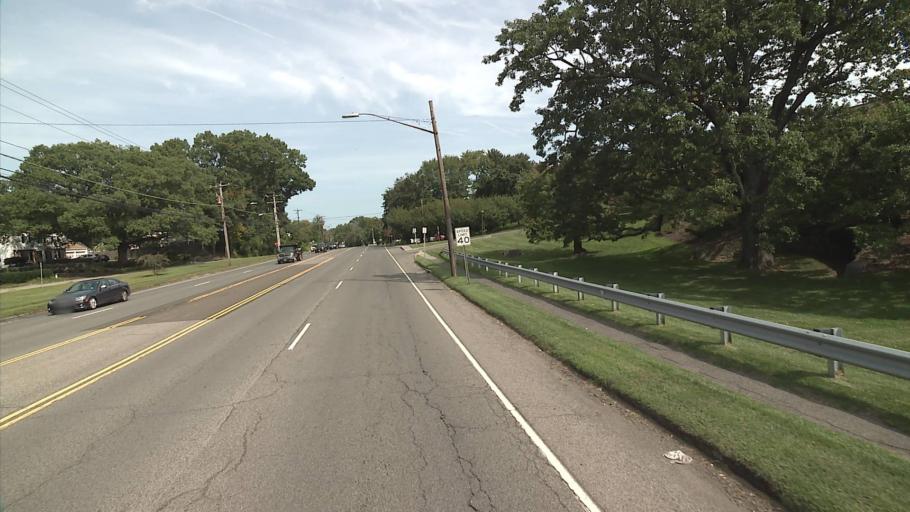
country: US
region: Connecticut
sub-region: Fairfield County
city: Stamford
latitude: 41.0805
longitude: -73.5497
